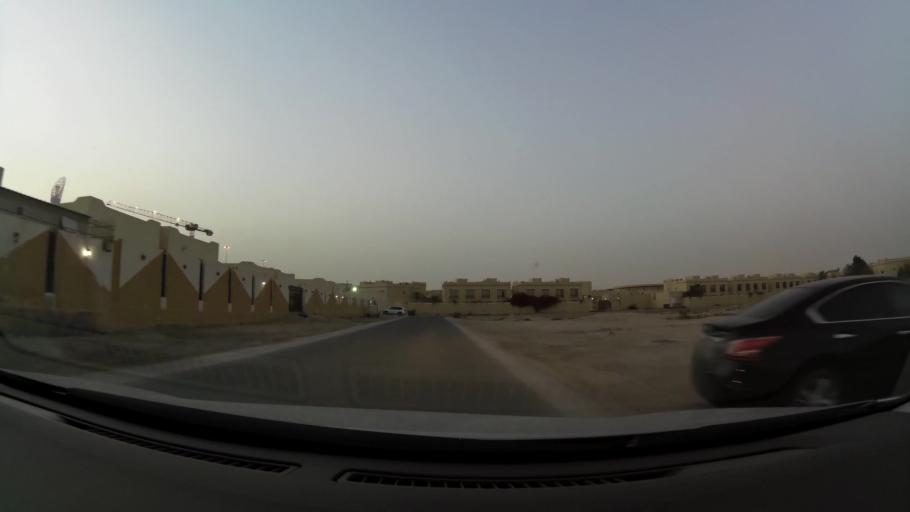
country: QA
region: Baladiyat ar Rayyan
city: Ar Rayyan
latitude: 25.2595
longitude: 51.4566
